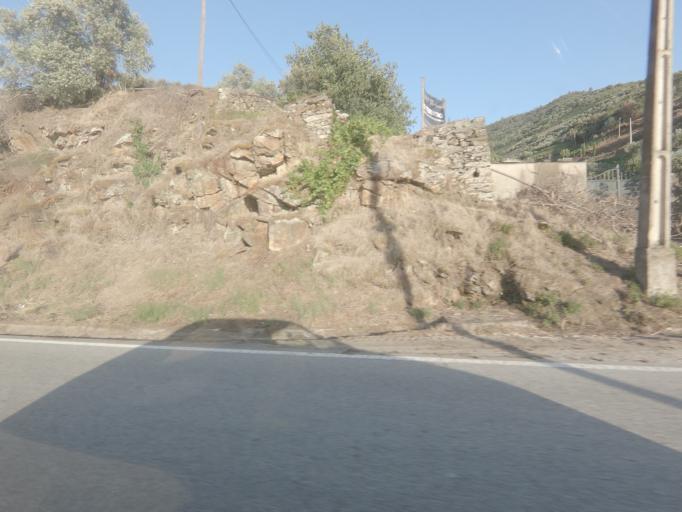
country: PT
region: Viseu
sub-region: Armamar
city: Armamar
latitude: 41.1566
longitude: -7.6732
